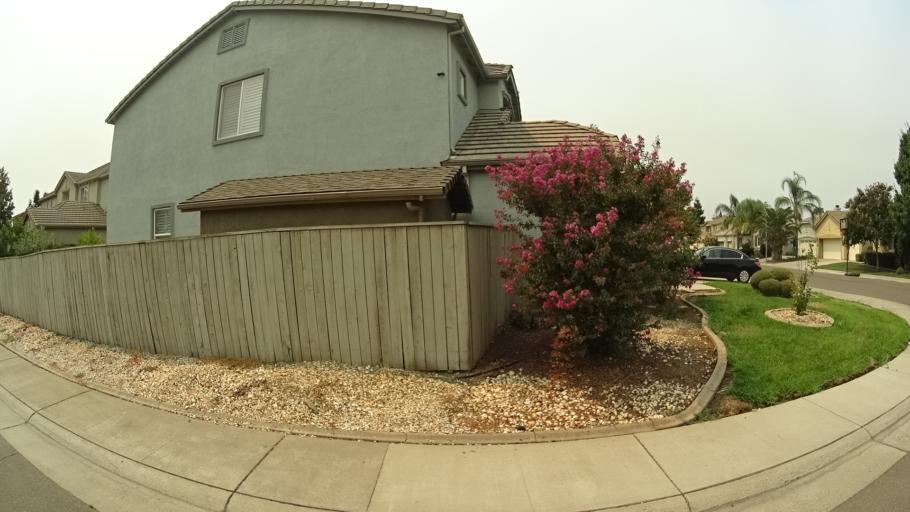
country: US
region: California
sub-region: Sacramento County
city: Laguna
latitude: 38.4001
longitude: -121.4216
